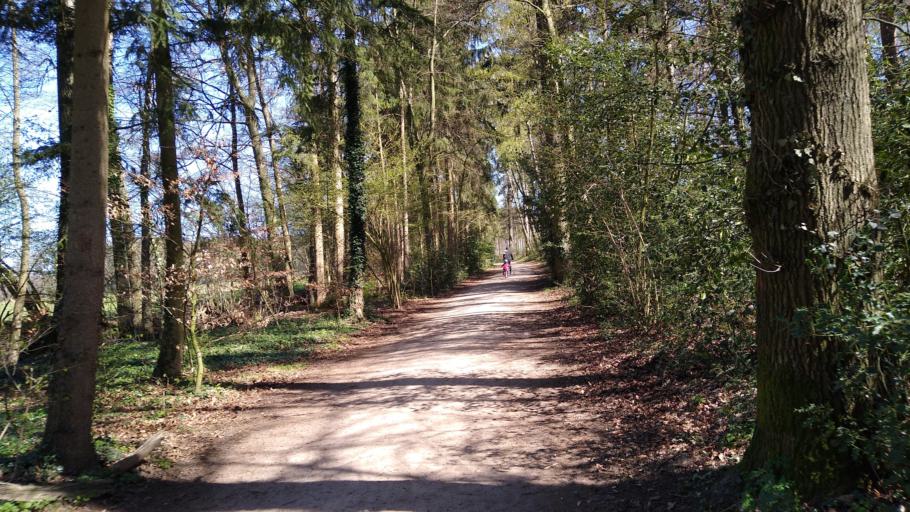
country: DE
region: North Rhine-Westphalia
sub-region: Regierungsbezirk Detmold
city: Verl
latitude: 51.8929
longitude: 8.5362
